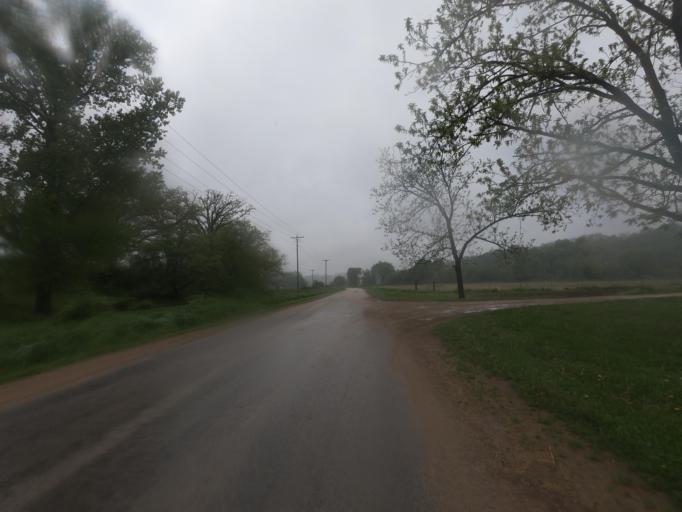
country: US
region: Wisconsin
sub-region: Grant County
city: Hazel Green
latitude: 42.5092
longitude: -90.4704
